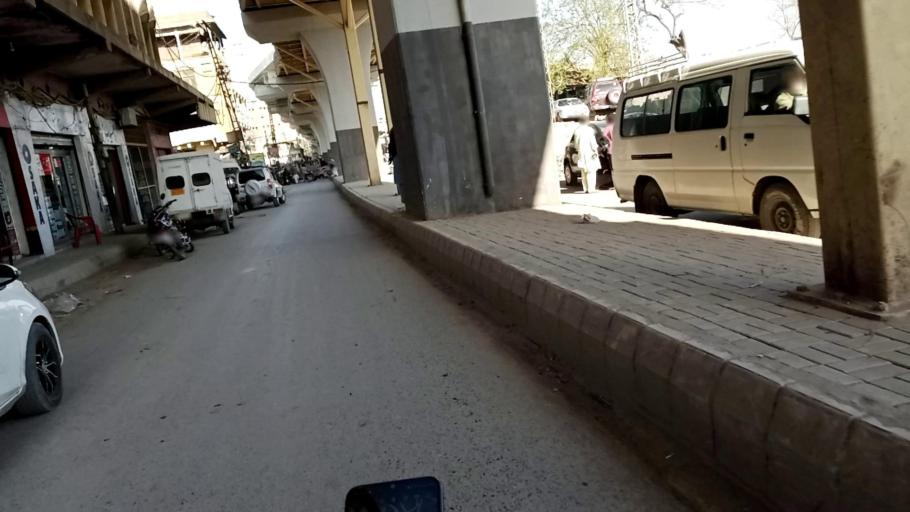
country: PK
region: Khyber Pakhtunkhwa
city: Peshawar
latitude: 34.0071
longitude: 71.5598
